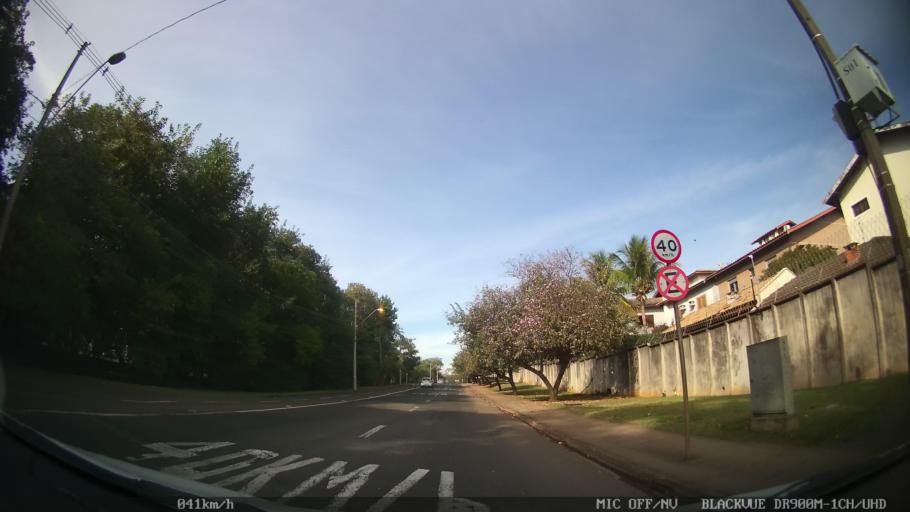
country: BR
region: Sao Paulo
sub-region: Piracicaba
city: Piracicaba
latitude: -22.7293
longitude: -47.6726
